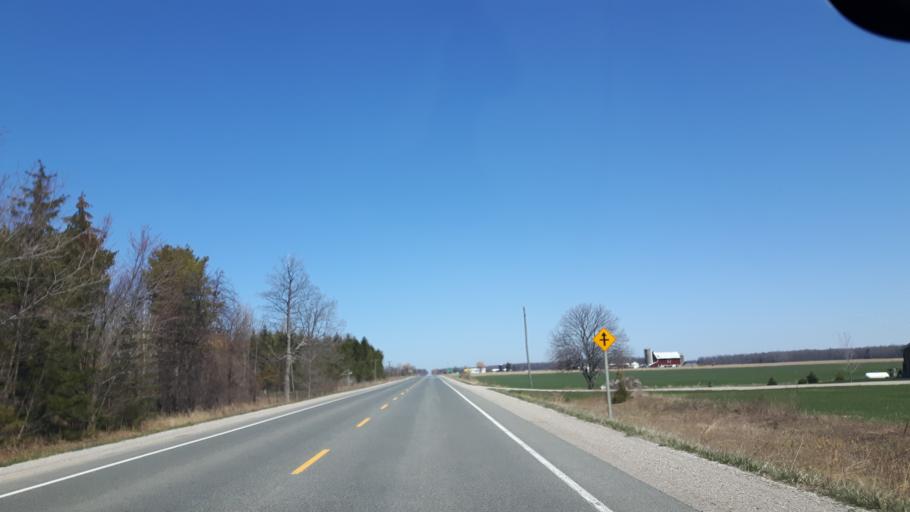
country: CA
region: Ontario
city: Goderich
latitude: 43.6212
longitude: -81.7056
